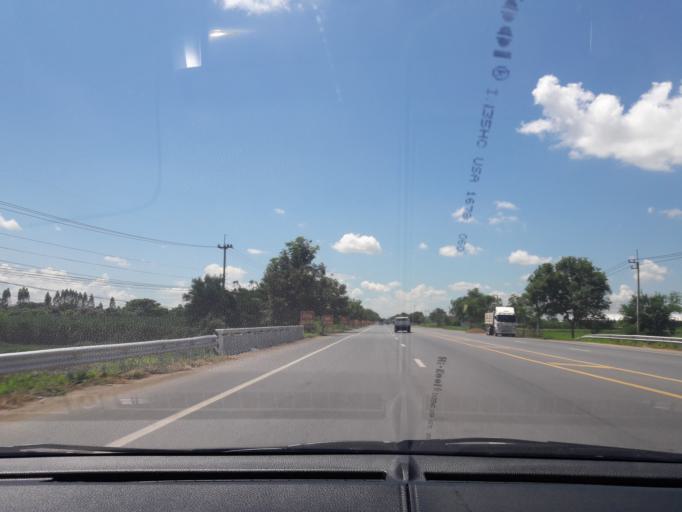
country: TH
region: Kanchanaburi
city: Tha Maka
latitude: 14.0318
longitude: 99.8304
